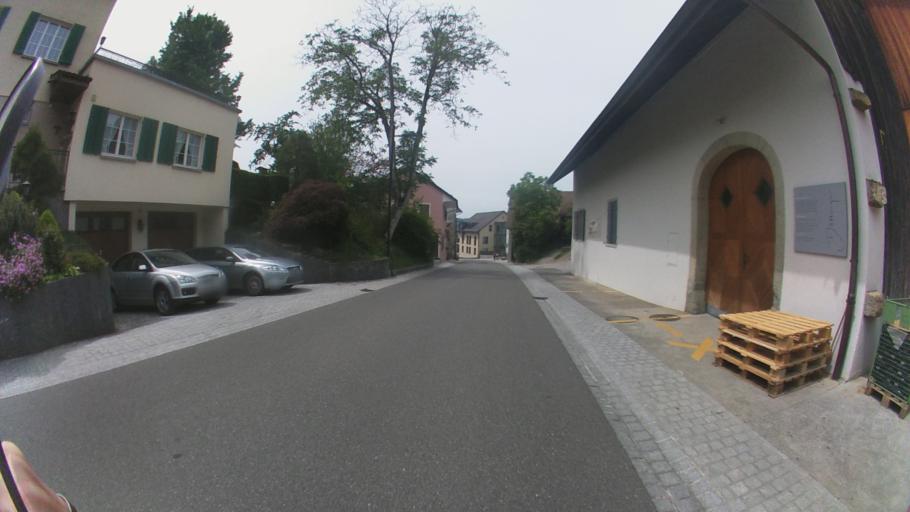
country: CH
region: Aargau
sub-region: Bezirk Zurzach
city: Klingnau
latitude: 47.5707
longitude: 8.2599
